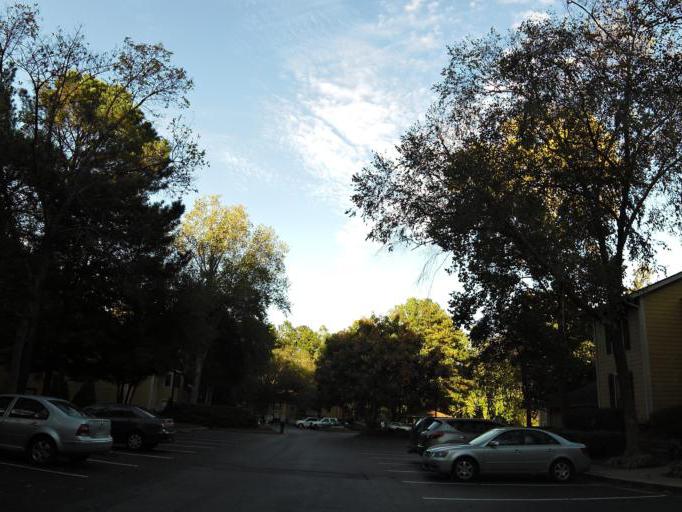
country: US
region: Georgia
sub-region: Cobb County
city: Vinings
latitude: 33.9063
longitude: -84.4516
